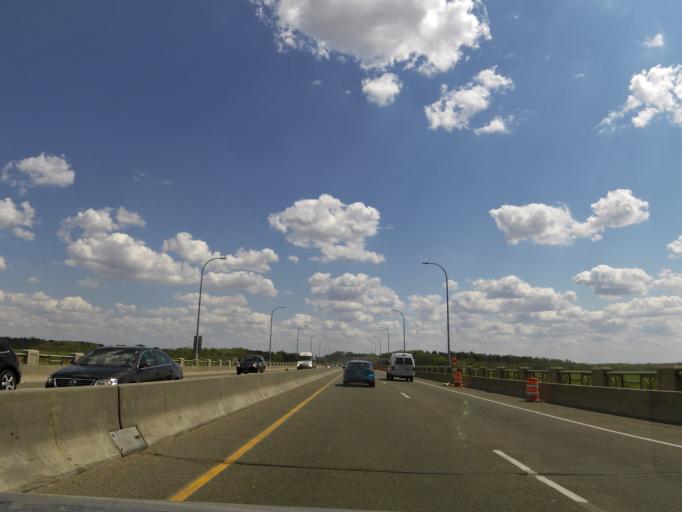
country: US
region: Minnesota
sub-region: Dakota County
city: Mendota Heights
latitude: 44.8901
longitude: -93.1826
